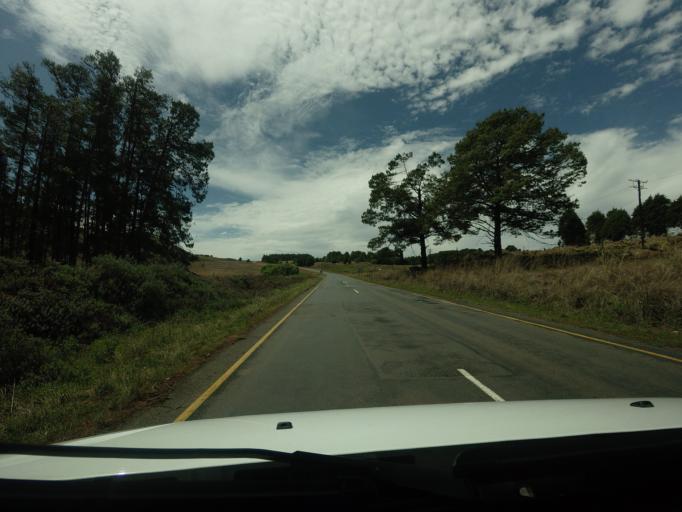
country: ZA
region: Mpumalanga
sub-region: Nkangala District Municipality
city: Belfast
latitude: -25.4126
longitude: 30.1141
